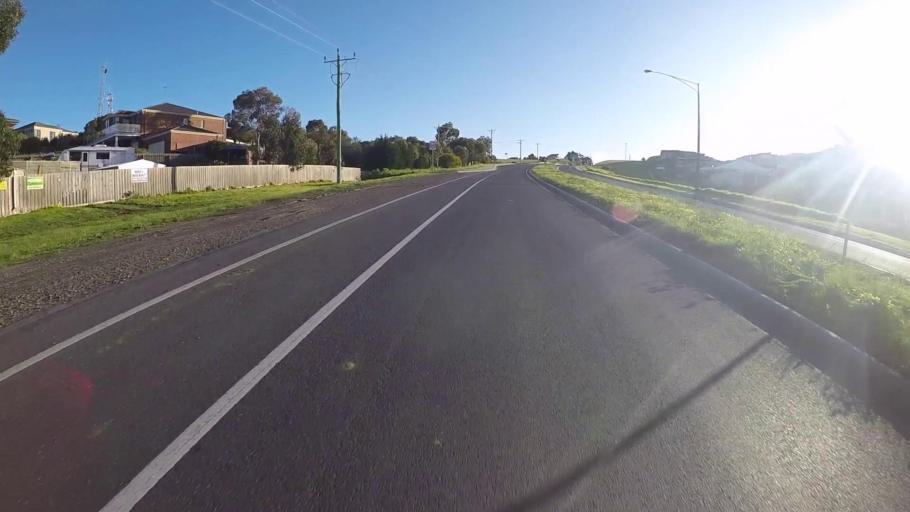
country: AU
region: Victoria
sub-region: Greater Geelong
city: Wandana Heights
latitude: -38.1711
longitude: 144.3006
